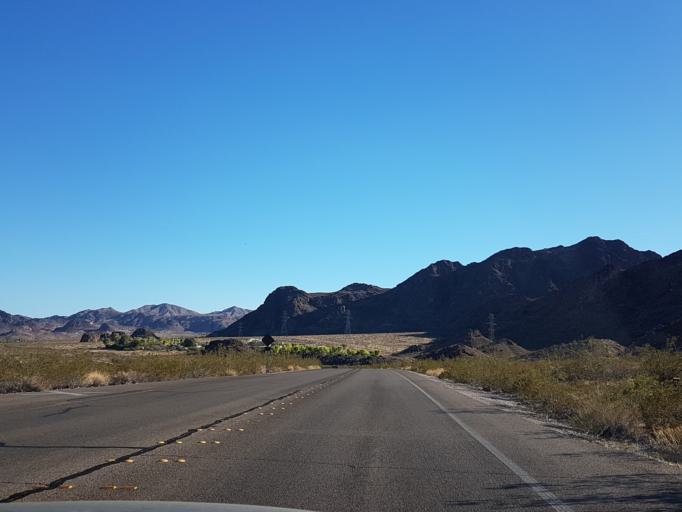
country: US
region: Nevada
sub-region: Clark County
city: Boulder City
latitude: 36.0524
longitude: -114.8195
